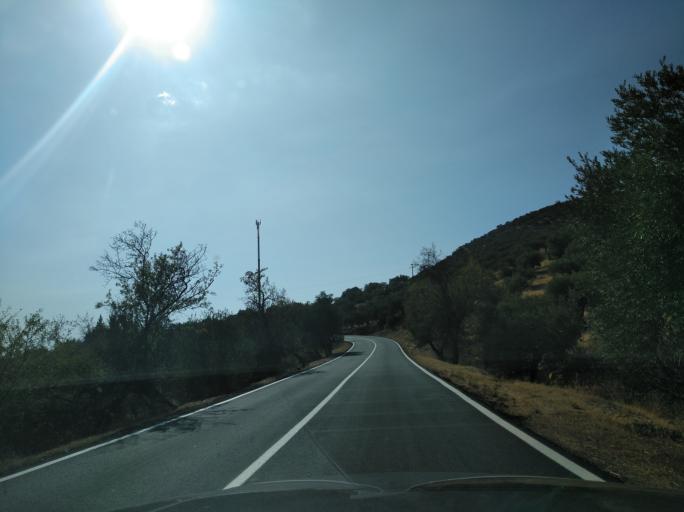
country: ES
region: Andalusia
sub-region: Provincia de Huelva
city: Rosal de la Frontera
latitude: 37.9558
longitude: -7.2699
